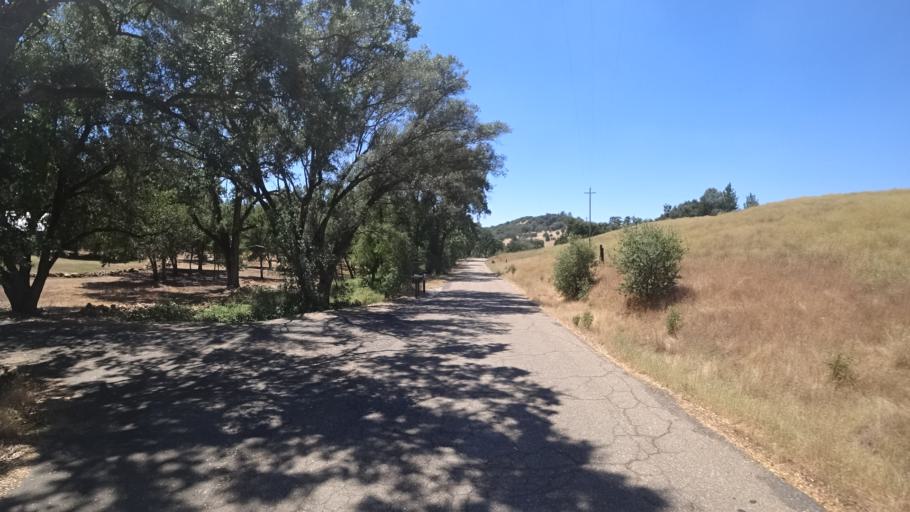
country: US
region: California
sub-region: Calaveras County
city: Angels Camp
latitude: 38.0914
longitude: -120.4990
